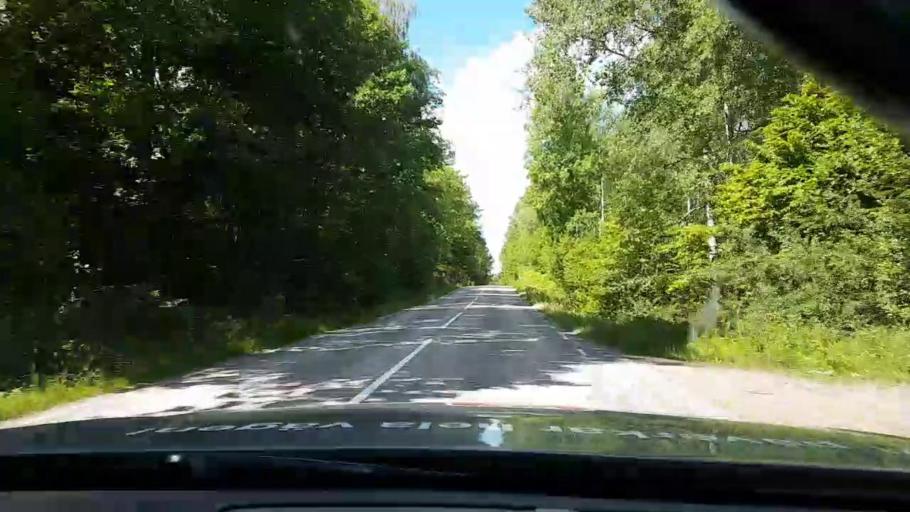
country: SE
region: Kalmar
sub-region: Vasterviks Kommun
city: Overum
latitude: 58.0696
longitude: 16.3866
